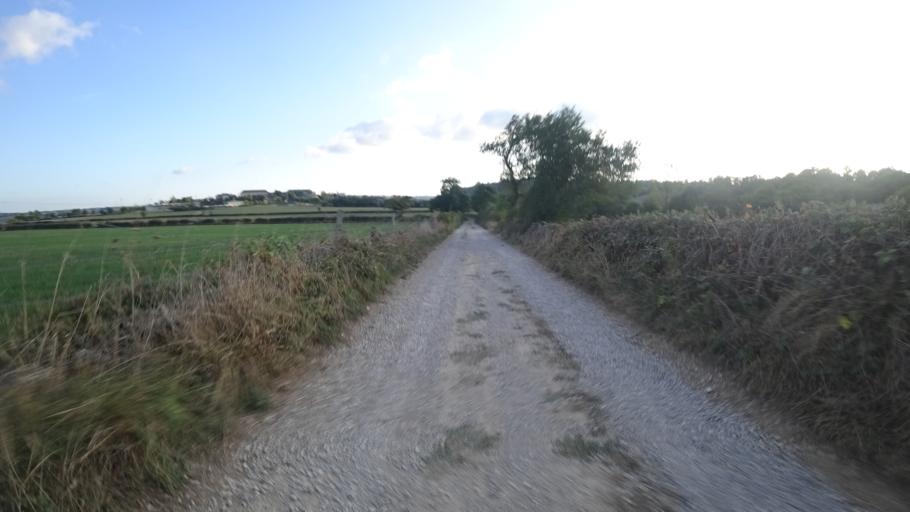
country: FR
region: Midi-Pyrenees
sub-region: Departement de l'Aveyron
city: Sebazac-Concoures
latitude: 44.3885
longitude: 2.5866
